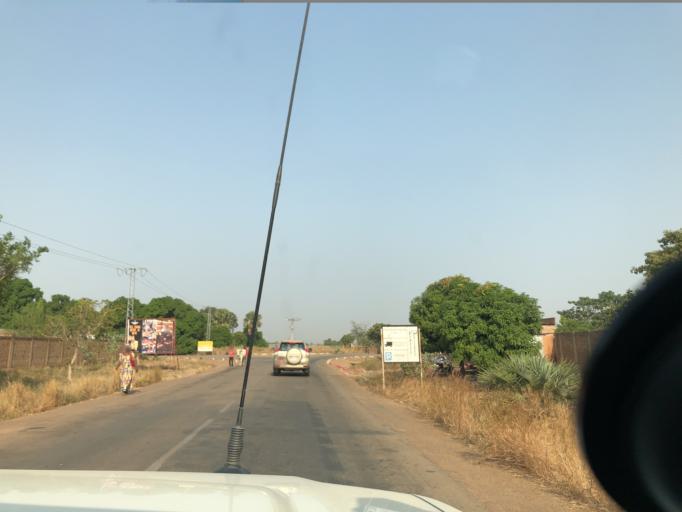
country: TD
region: Logone Occidental
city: Moundou
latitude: 8.5864
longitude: 16.0234
